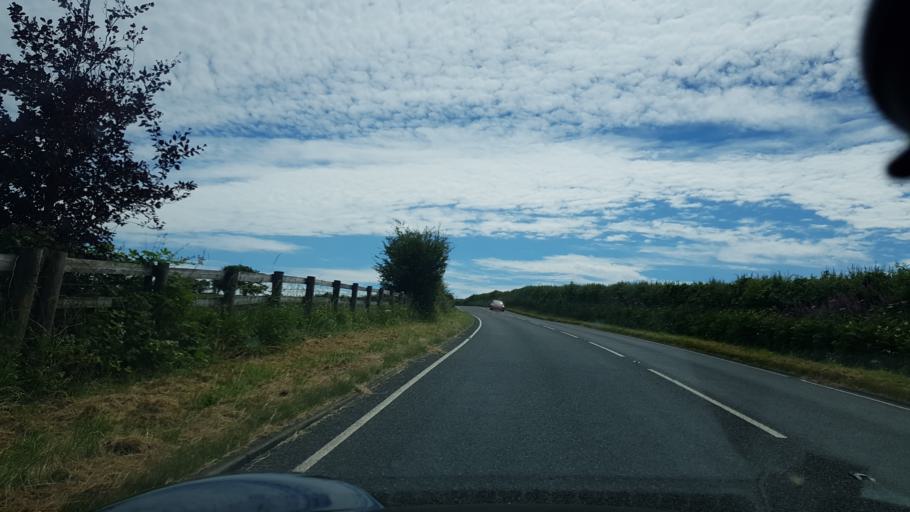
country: GB
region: Wales
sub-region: Carmarthenshire
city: Saint Clears
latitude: 51.7890
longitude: -4.4821
